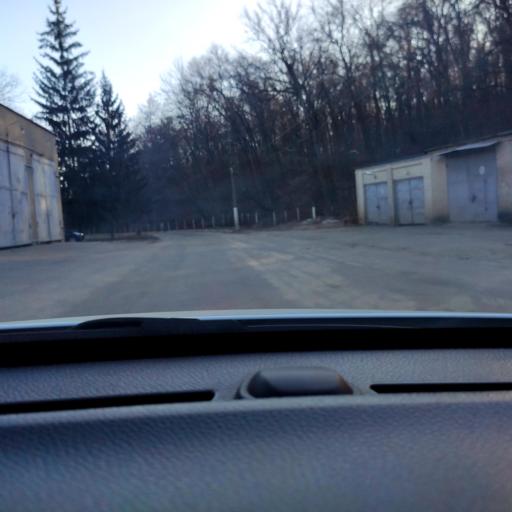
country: RU
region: Voronezj
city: Voronezh
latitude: 51.7270
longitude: 39.2293
